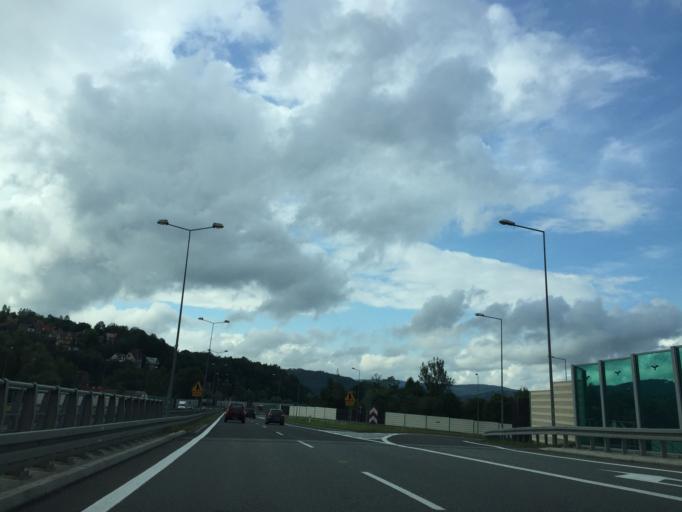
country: PL
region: Lesser Poland Voivodeship
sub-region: Powiat myslenicki
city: Lubien
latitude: 49.7188
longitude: 19.9813
